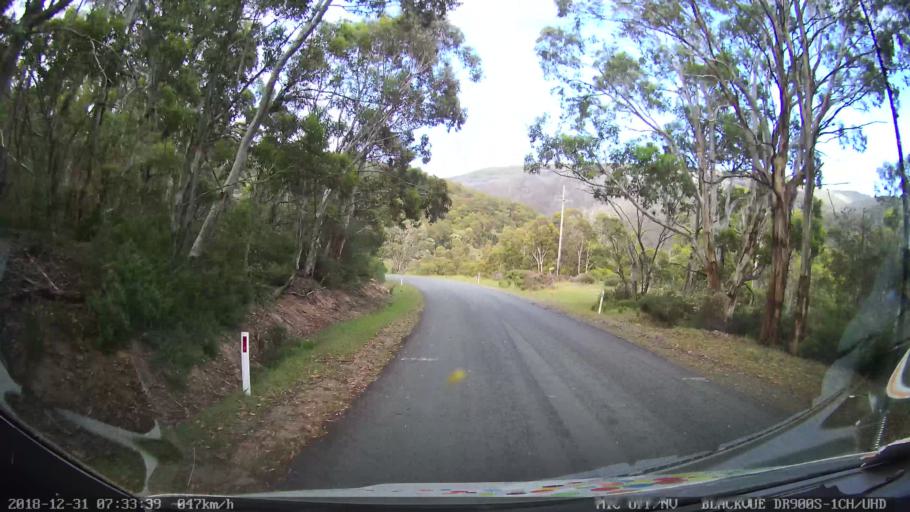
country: AU
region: New South Wales
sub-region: Snowy River
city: Jindabyne
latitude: -36.3330
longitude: 148.4556
